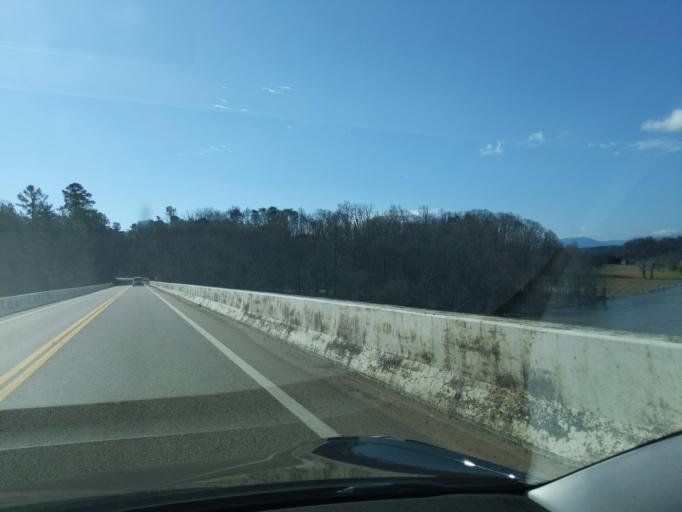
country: US
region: Tennessee
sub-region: Sevier County
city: Sevierville
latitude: 35.9580
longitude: -83.5471
